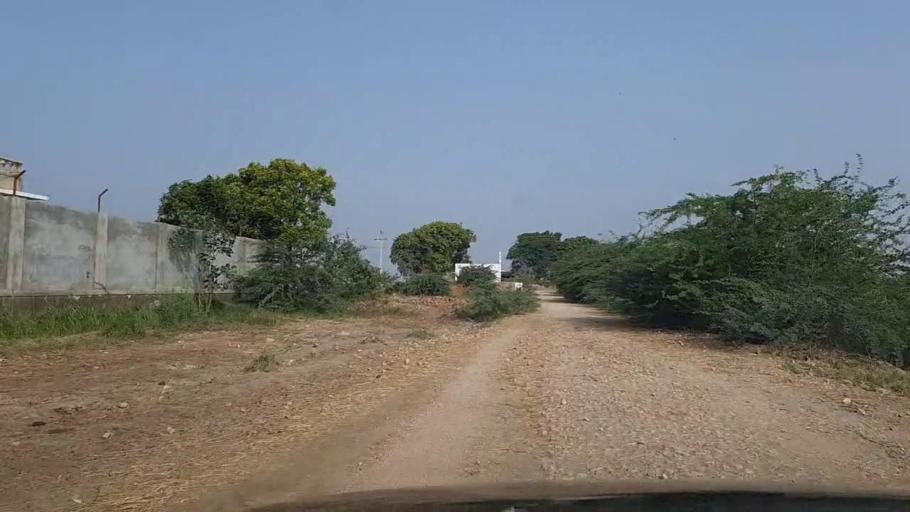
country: PK
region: Sindh
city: Thatta
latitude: 24.7674
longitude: 67.8709
